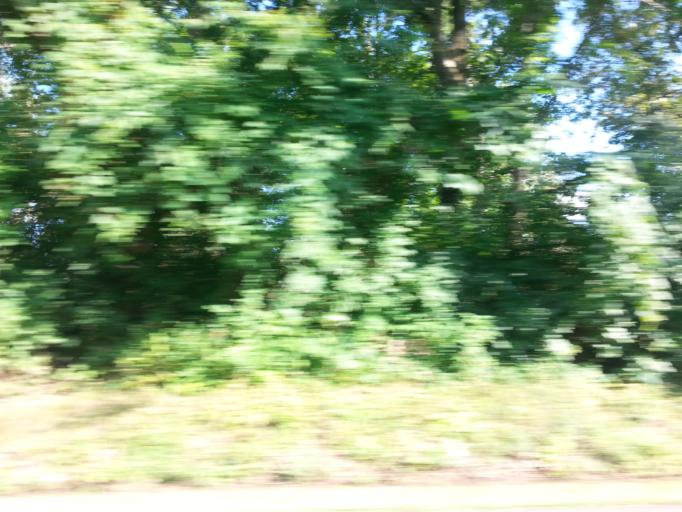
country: US
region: Tennessee
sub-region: Loudon County
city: Greenback
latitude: 35.6677
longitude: -84.0710
